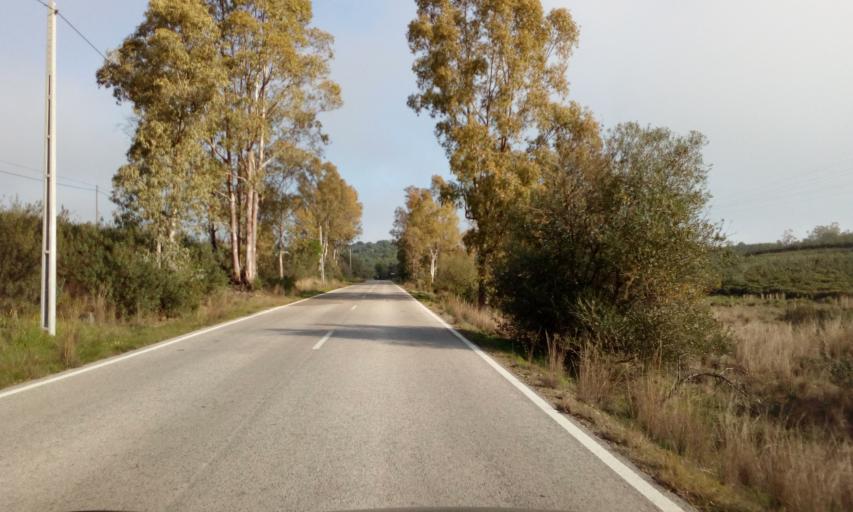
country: PT
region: Faro
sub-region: Alcoutim
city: Alcoutim
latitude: 37.4492
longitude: -7.4889
